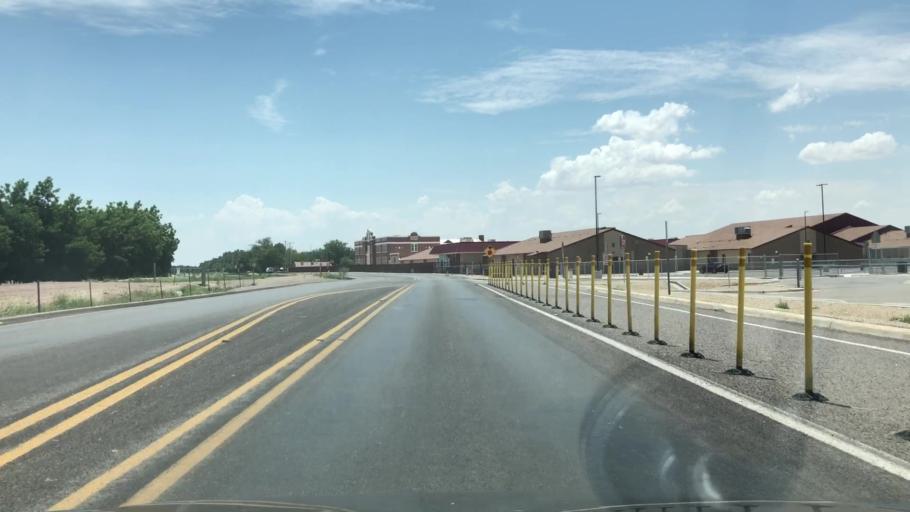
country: US
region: New Mexico
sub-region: Dona Ana County
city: La Union
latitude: 31.9997
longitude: -106.6564
